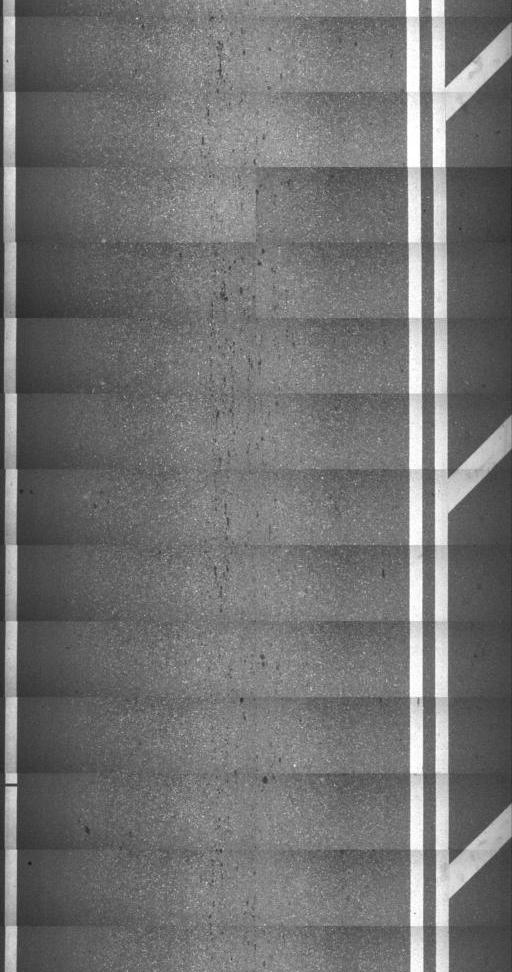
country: US
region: Vermont
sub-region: Caledonia County
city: St Johnsbury
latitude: 44.4295
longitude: -72.0180
